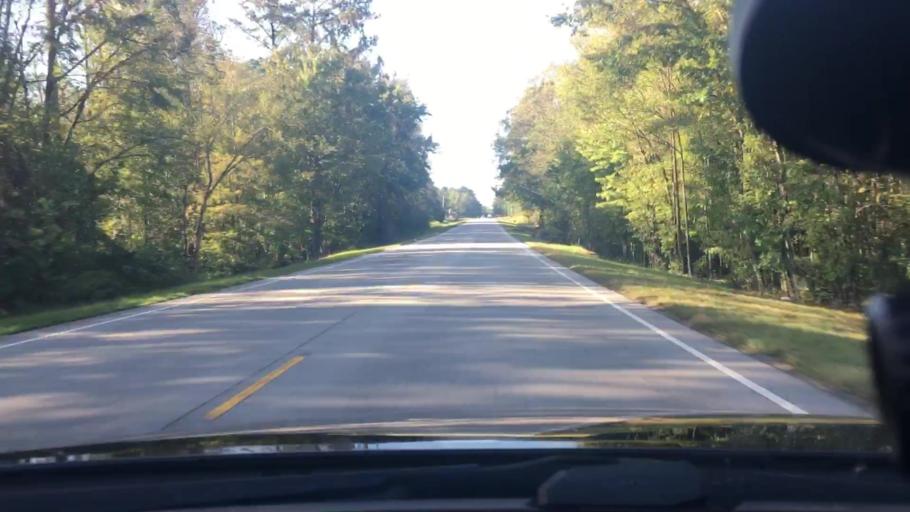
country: US
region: North Carolina
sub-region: Craven County
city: Vanceboro
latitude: 35.3132
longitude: -77.1403
